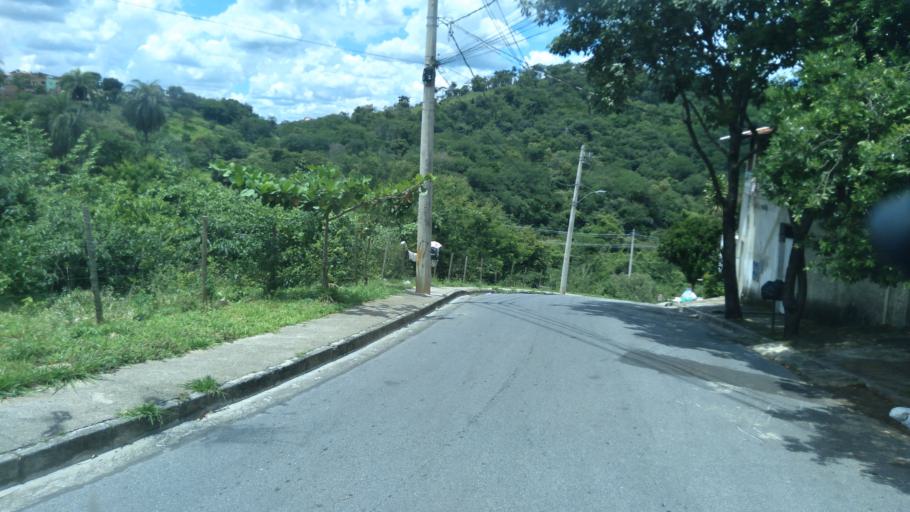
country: BR
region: Minas Gerais
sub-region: Belo Horizonte
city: Belo Horizonte
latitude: -19.8564
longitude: -43.8753
